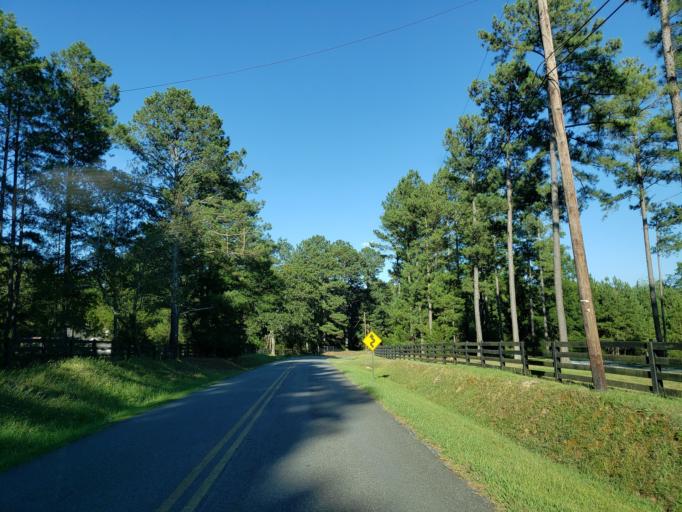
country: US
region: Georgia
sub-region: Bartow County
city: Euharlee
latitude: 34.1263
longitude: -84.9892
